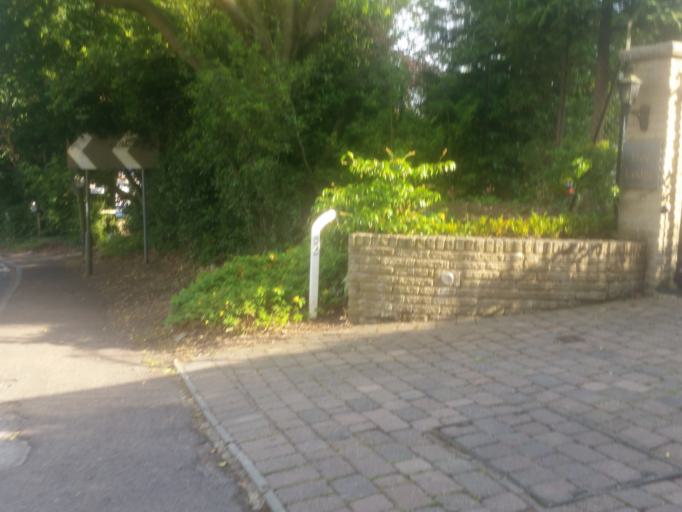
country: GB
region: England
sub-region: Greater London
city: High Barnet
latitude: 51.6411
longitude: -0.2420
